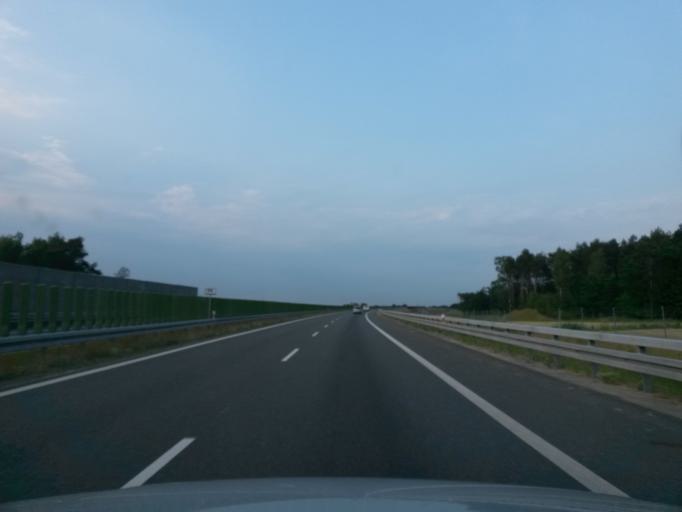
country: PL
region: Lower Silesian Voivodeship
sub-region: Powiat olesnicki
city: Miedzyborz
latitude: 51.2953
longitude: 17.5830
